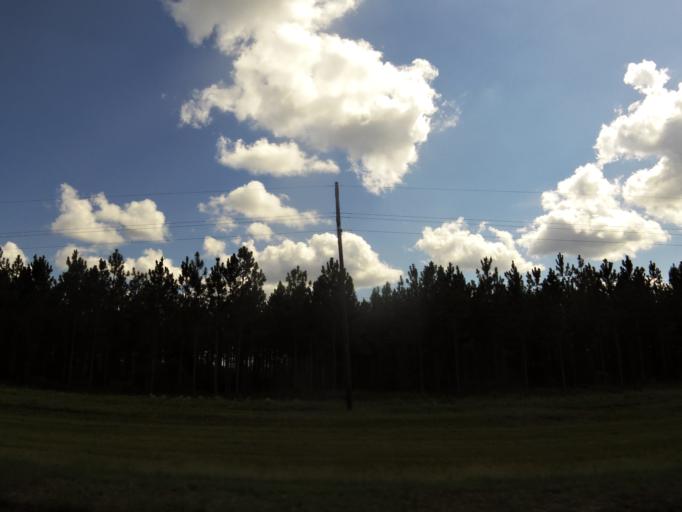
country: US
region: Florida
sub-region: Hamilton County
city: Jasper
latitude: 30.6746
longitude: -82.6430
